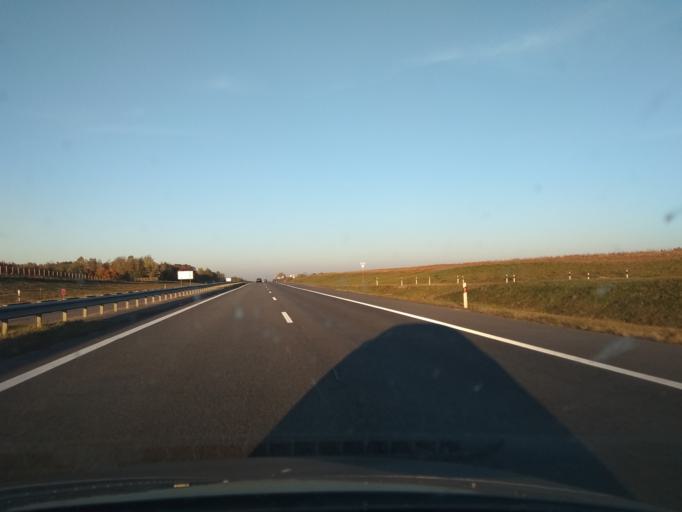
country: BY
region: Brest
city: Baranovichi
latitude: 53.1962
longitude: 26.0850
